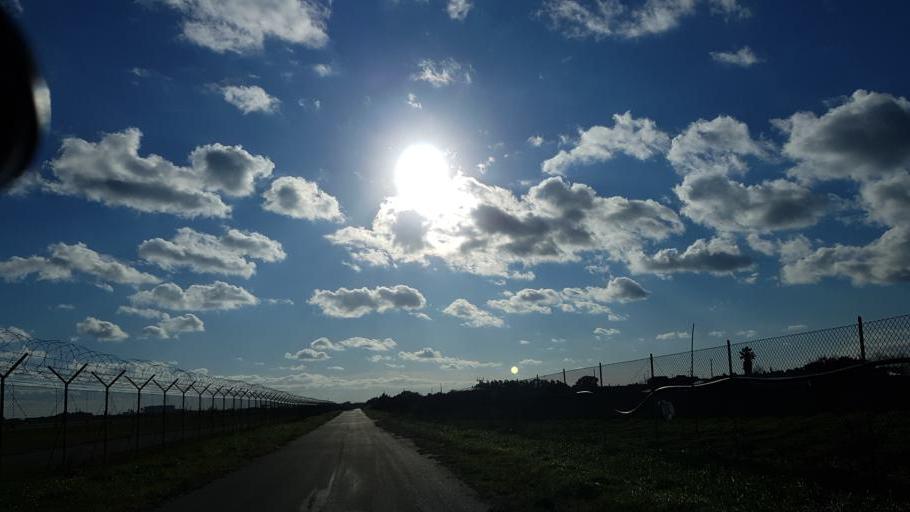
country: IT
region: Apulia
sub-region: Provincia di Brindisi
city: Materdomini
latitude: 40.6661
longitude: 17.9346
